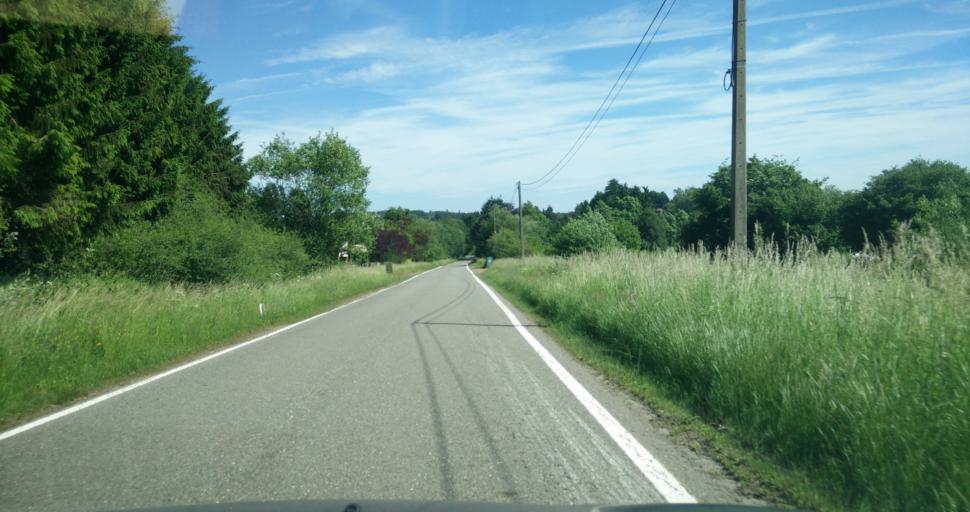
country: BE
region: Wallonia
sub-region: Province du Luxembourg
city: La Roche-en-Ardenne
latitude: 50.2279
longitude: 5.6241
